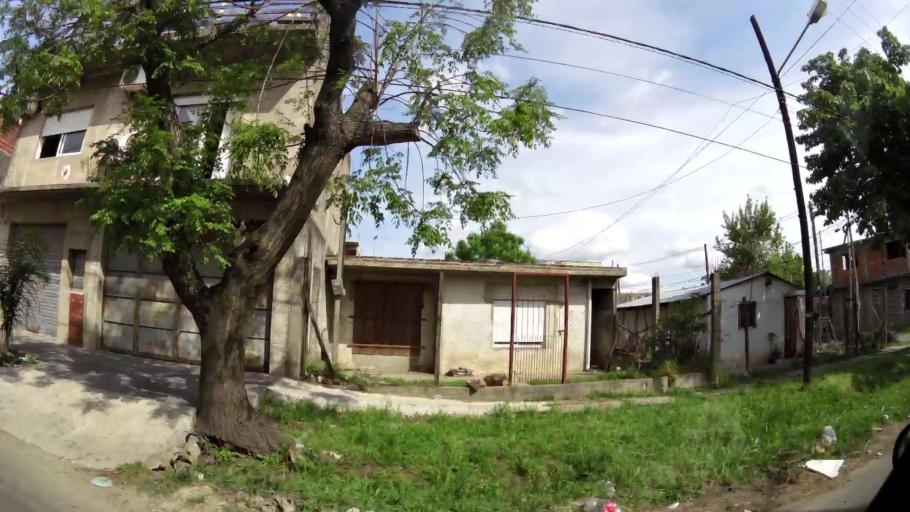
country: AR
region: Buenos Aires
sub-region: Partido de Quilmes
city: Quilmes
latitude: -34.7637
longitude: -58.2397
